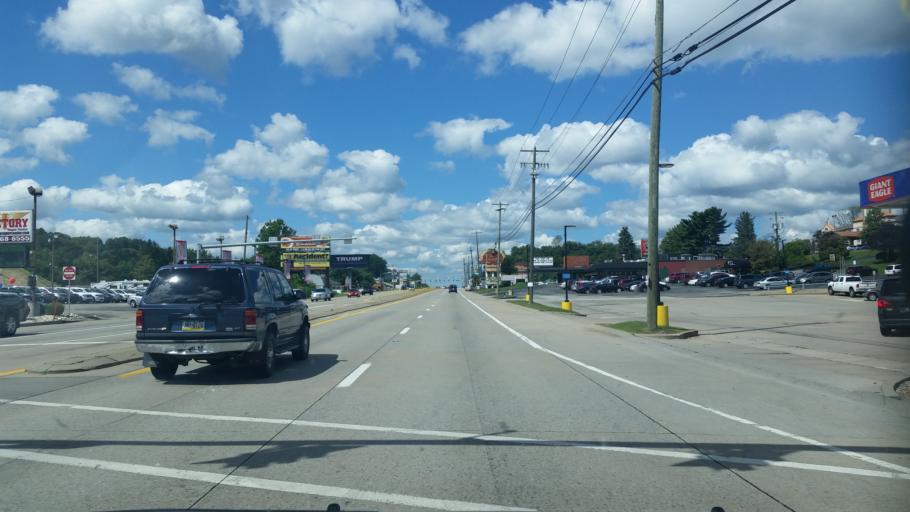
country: US
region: Pennsylvania
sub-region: Westmoreland County
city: Delmont
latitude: 40.3992
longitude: -79.5796
